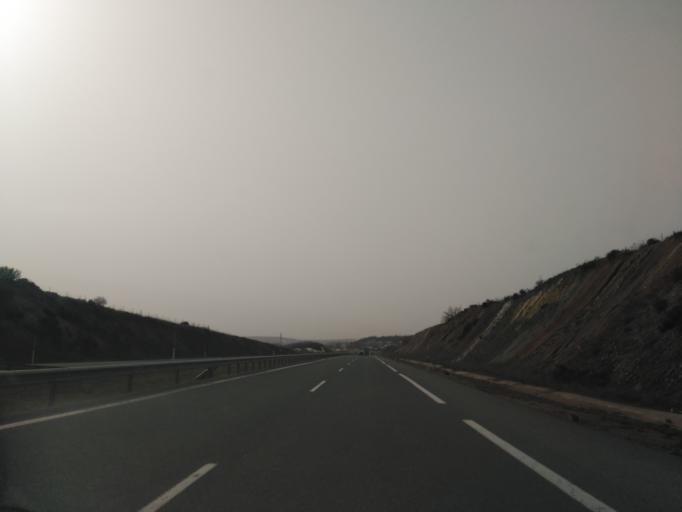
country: ES
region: Cantabria
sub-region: Provincia de Cantabria
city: Mataporquera
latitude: 42.8318
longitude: -4.1995
